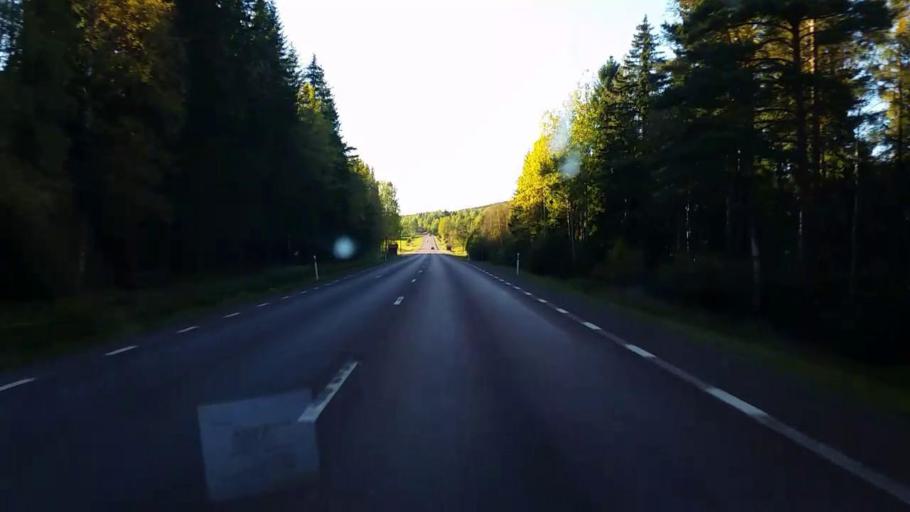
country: SE
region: Gaevleborg
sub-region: Ljusdals Kommun
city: Jaervsoe
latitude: 61.8147
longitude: 16.1995
